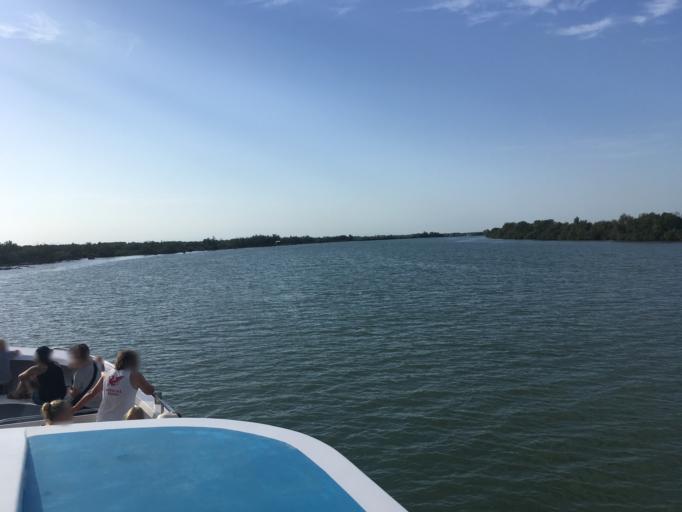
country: FR
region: Provence-Alpes-Cote d'Azur
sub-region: Departement des Bouches-du-Rhone
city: Saintes-Maries-de-la-Mer
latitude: 43.4677
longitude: 4.3807
